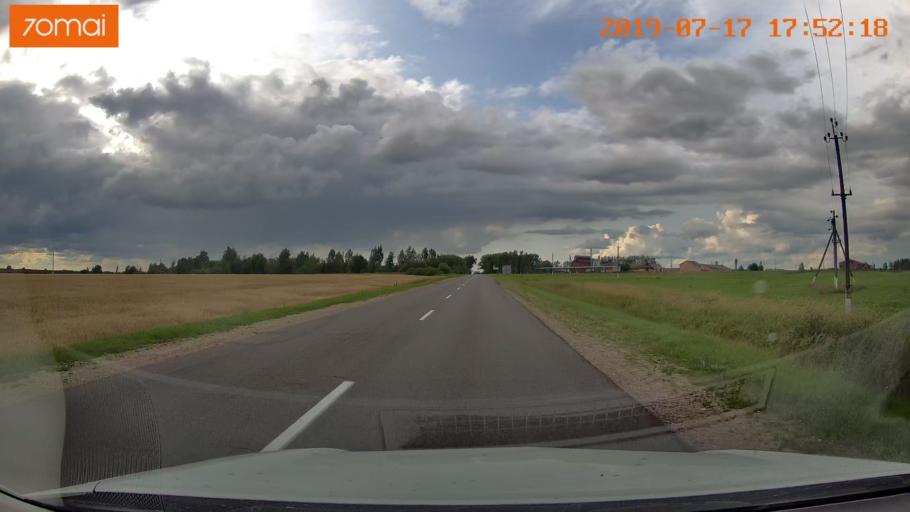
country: BY
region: Mogilev
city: Hlusha
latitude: 53.1637
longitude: 28.7834
